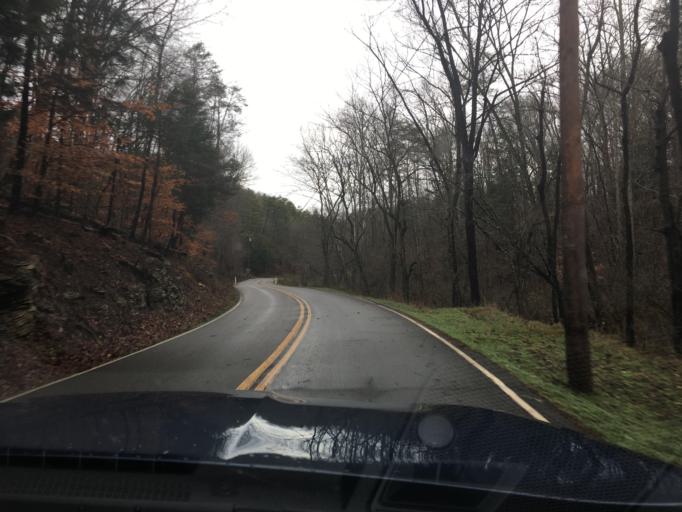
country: US
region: Tennessee
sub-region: McMinn County
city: Englewood
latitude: 35.3668
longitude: -84.4366
